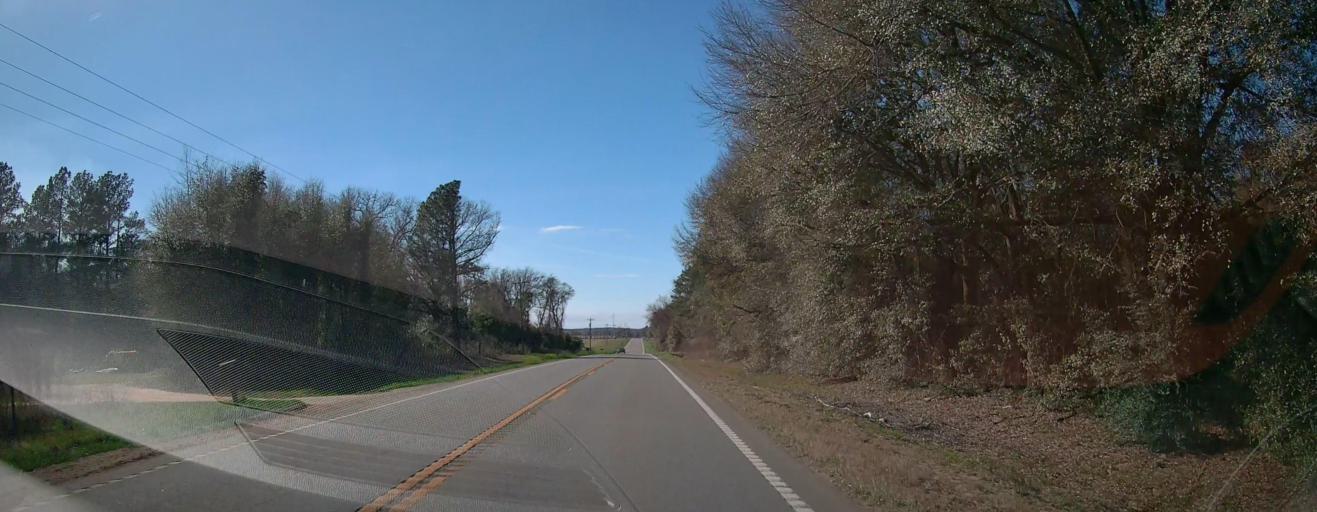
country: US
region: Georgia
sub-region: Macon County
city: Oglethorpe
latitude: 32.3323
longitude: -84.1031
